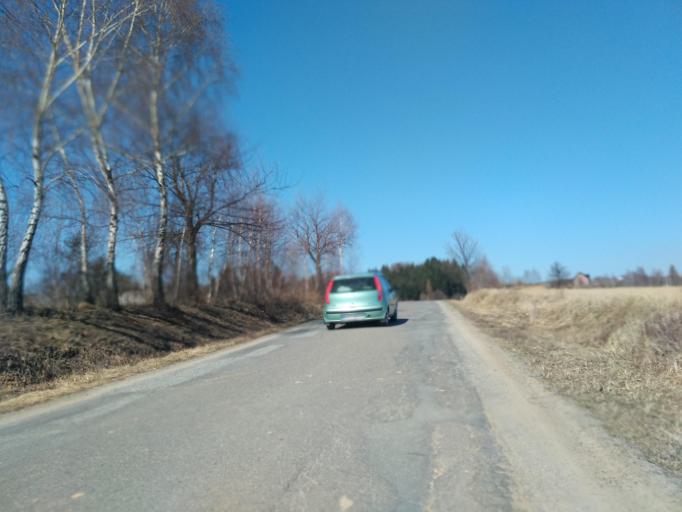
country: PL
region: Subcarpathian Voivodeship
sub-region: Powiat debicki
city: Brzostek
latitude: 49.9506
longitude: 21.4302
